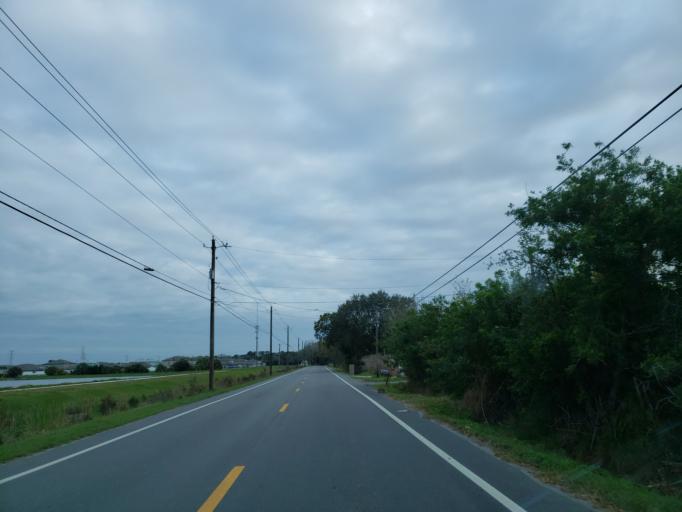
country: US
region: Florida
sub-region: Hillsborough County
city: Palm River-Clair Mel
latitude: 27.9145
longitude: -82.3769
